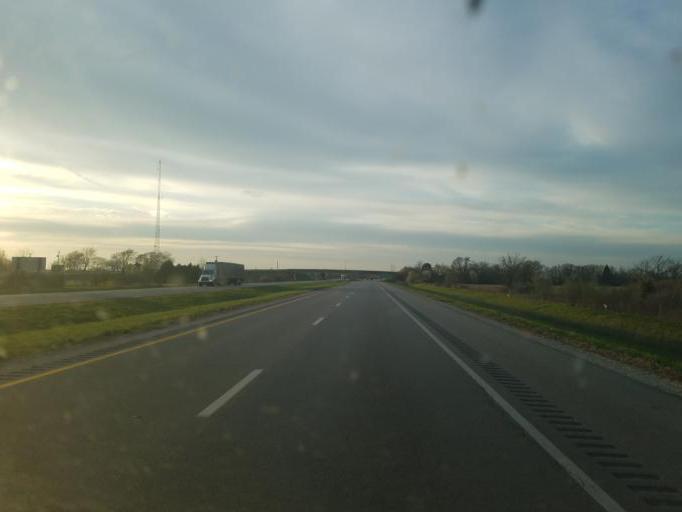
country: US
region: Ohio
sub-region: Wood County
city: Walbridge
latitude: 41.5759
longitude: -83.4708
